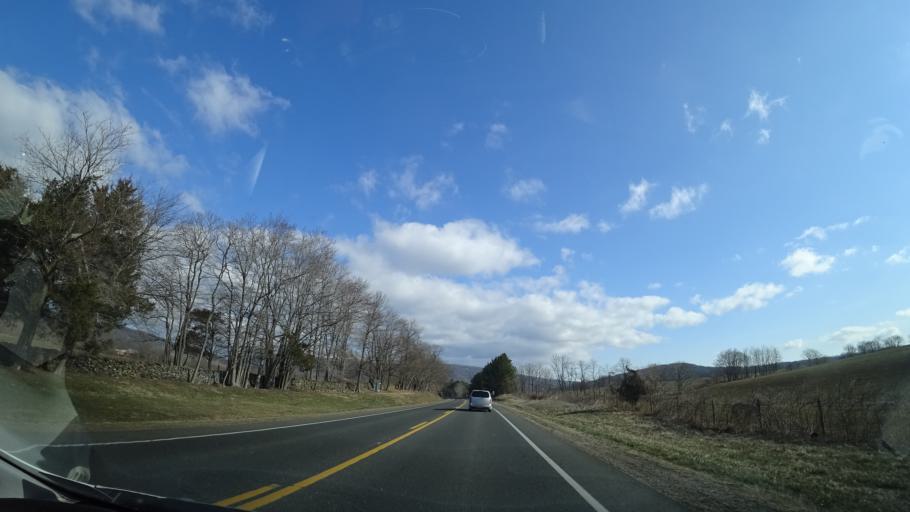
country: US
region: Virginia
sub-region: Warren County
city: Shenandoah Farms
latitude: 38.9808
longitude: -77.9503
